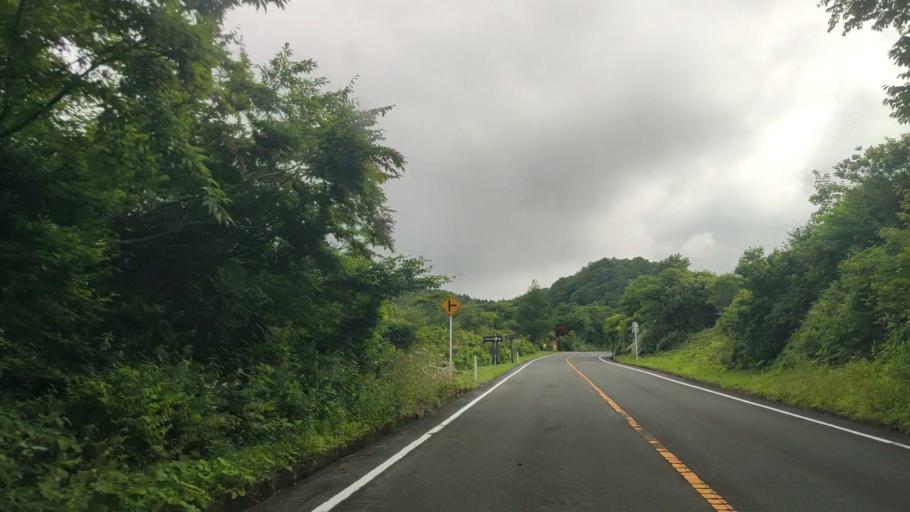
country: JP
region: Tottori
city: Kurayoshi
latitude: 35.3256
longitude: 133.5882
